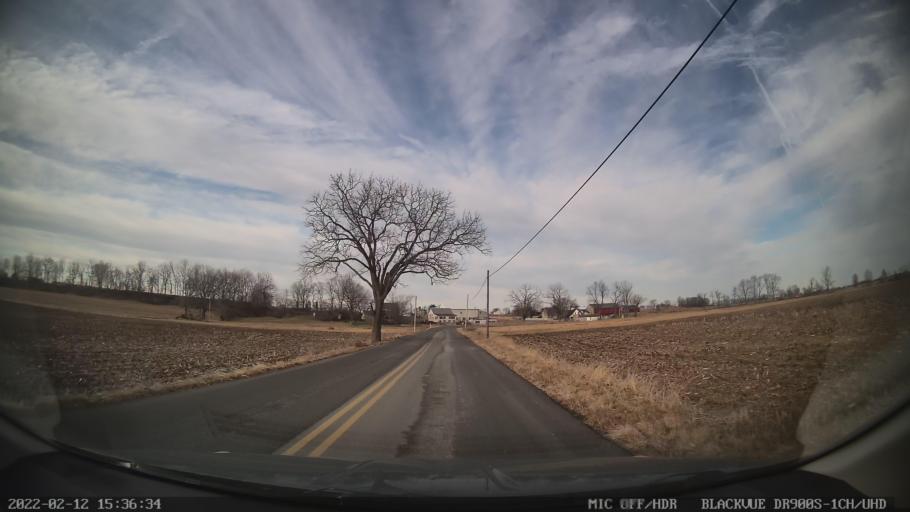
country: US
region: Pennsylvania
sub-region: Berks County
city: Topton
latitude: 40.4921
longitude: -75.7373
